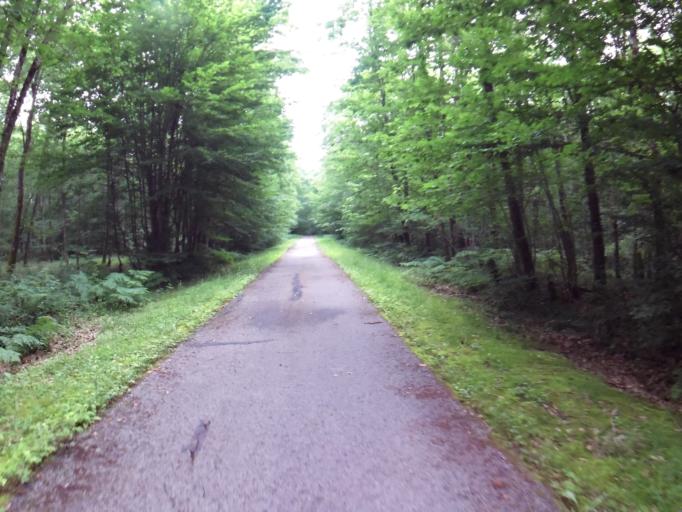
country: FR
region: Champagne-Ardenne
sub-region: Departement de la Haute-Marne
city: Montier-en-Der
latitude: 48.5309
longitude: 4.7716
